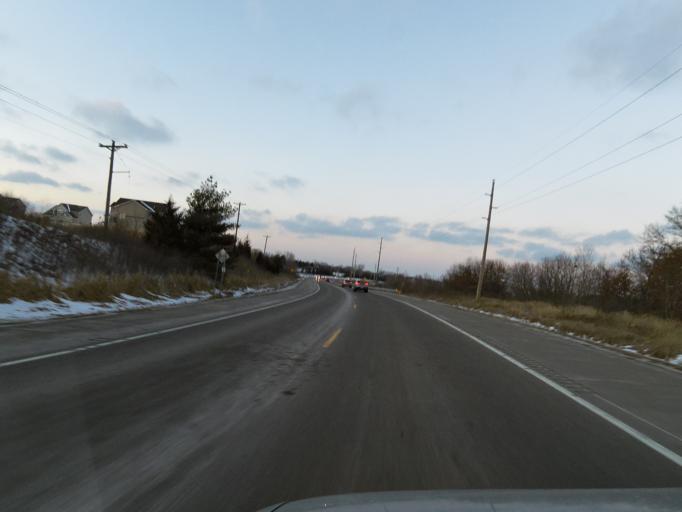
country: US
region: Minnesota
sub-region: Dakota County
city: Rosemount
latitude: 44.7762
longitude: -93.1169
